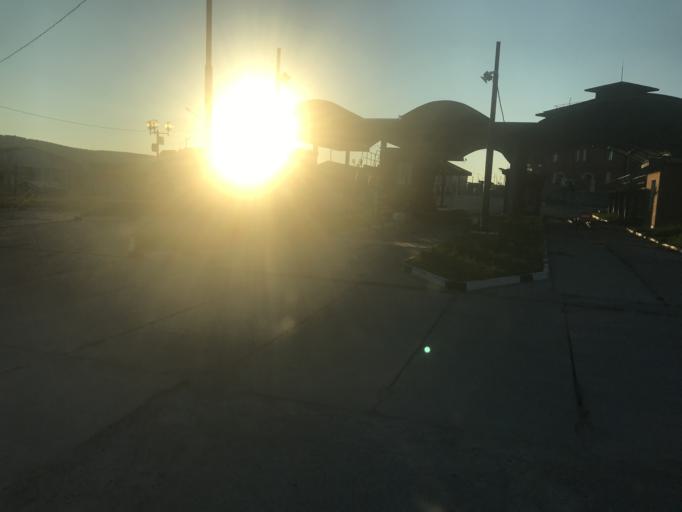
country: MN
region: Selenge
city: Altanbulag
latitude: 50.3249
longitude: 106.4880
